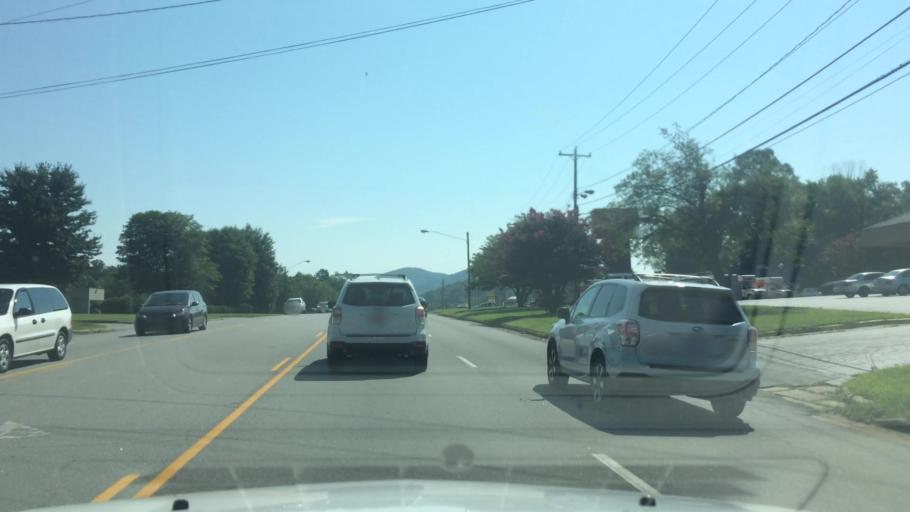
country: US
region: North Carolina
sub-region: Caldwell County
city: Lenoir
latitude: 35.9145
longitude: -81.5235
